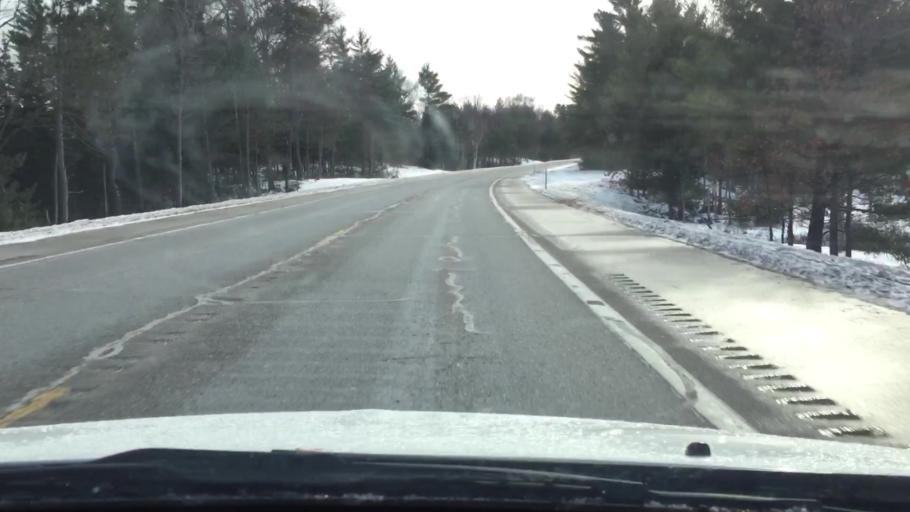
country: US
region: Michigan
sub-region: Wexford County
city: Manton
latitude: 44.5474
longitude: -85.3703
